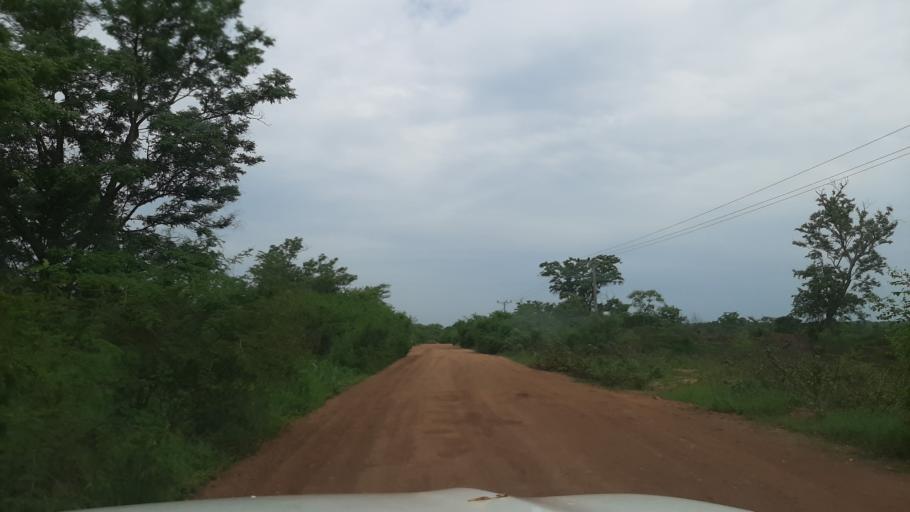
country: ET
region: Gambela
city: Gambela
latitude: 8.2151
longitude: 34.5612
